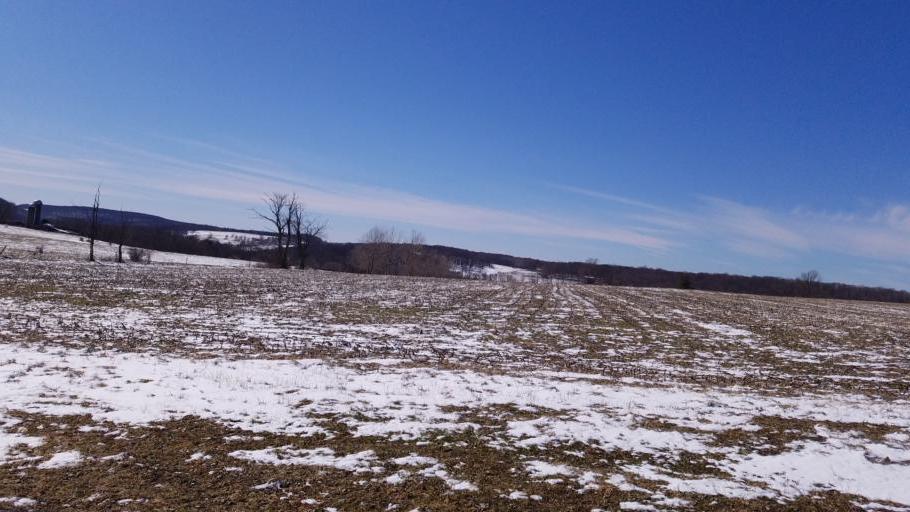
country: US
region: New York
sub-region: Allegany County
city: Wellsville
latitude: 41.9988
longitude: -77.9301
